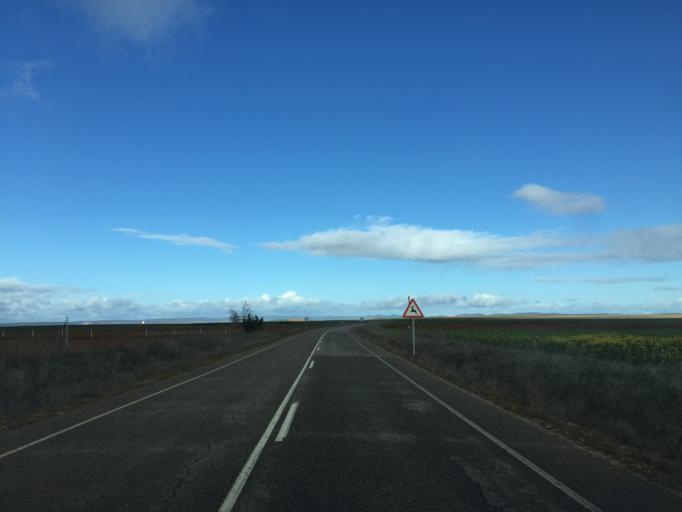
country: ES
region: Castille and Leon
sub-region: Provincia de Zamora
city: Manganeses de la Lampreana
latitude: 41.7567
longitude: -5.7224
